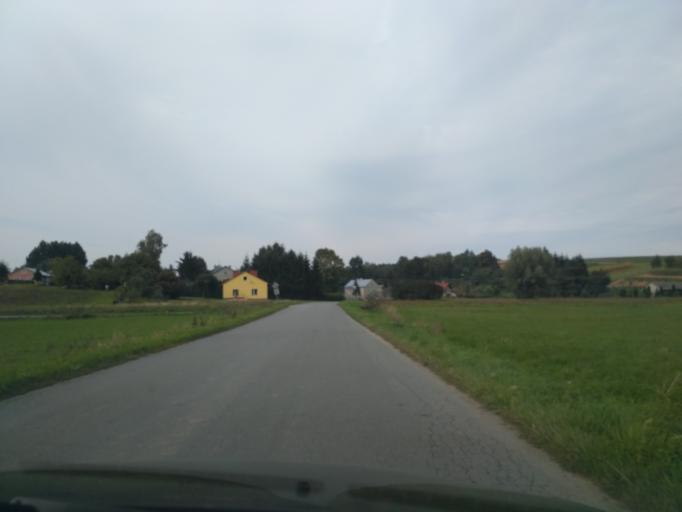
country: PL
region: Subcarpathian Voivodeship
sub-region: Powiat rzeszowski
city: Zglobien
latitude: 50.0323
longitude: 21.8433
